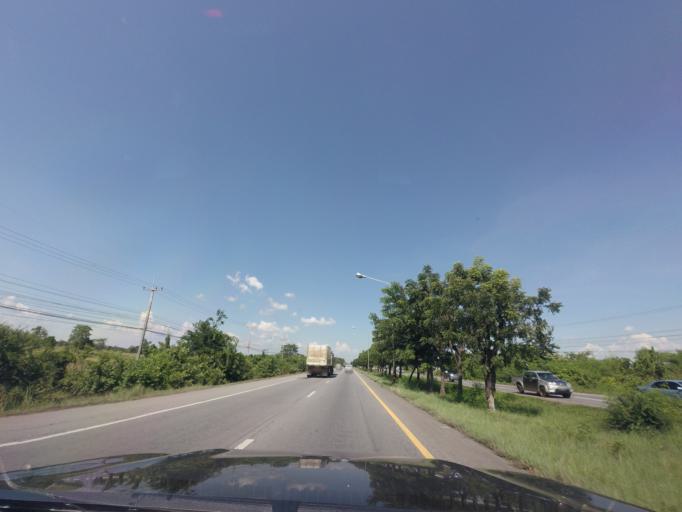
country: TH
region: Nakhon Ratchasima
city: Non Sung
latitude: 15.2245
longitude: 102.3649
